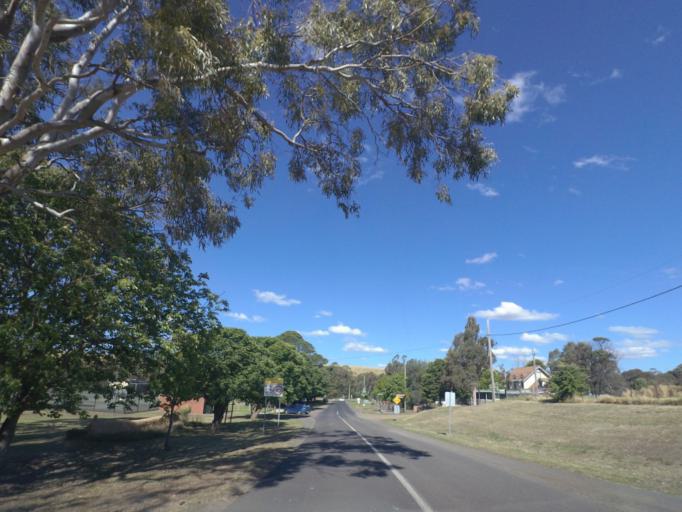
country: AU
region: Victoria
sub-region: Hume
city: Craigieburn
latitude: -37.4015
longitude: 144.8920
